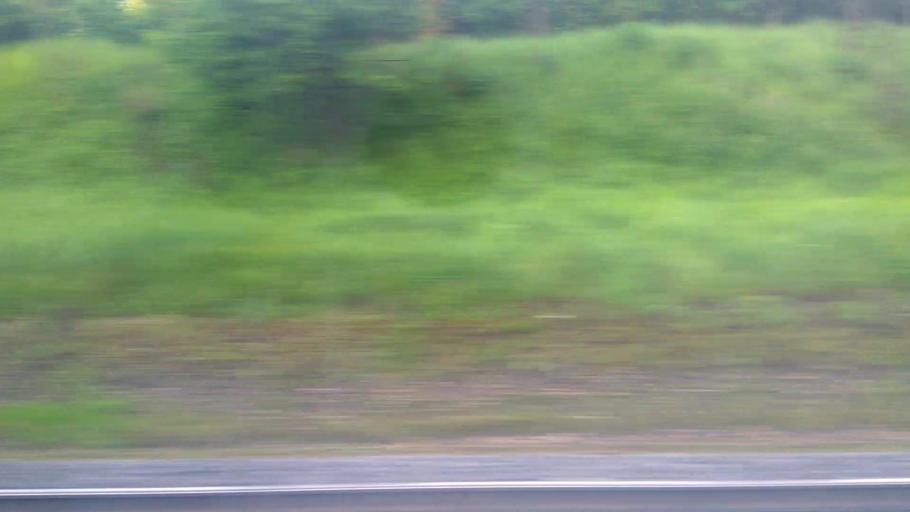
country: RU
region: Moskovskaya
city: Zhilevo
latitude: 54.9609
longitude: 38.0440
